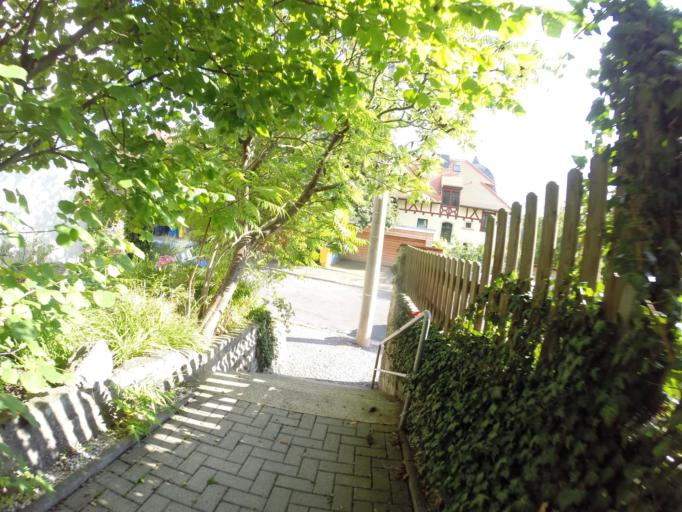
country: DE
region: Thuringia
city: Jena
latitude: 50.9354
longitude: 11.5719
